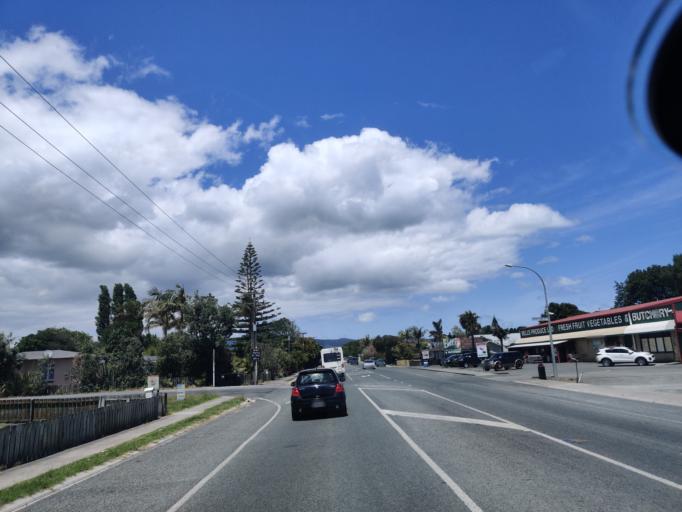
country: NZ
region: Northland
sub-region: Far North District
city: Kaitaia
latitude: -35.1006
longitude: 173.2597
